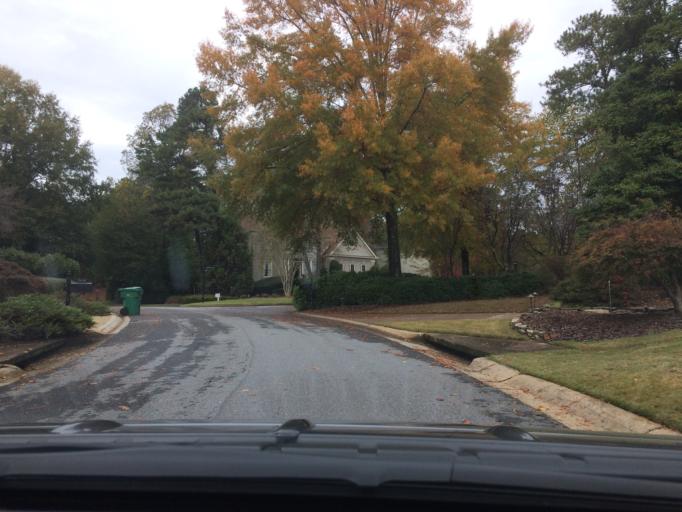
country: US
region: Georgia
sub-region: Fulton County
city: Johns Creek
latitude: 34.0092
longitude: -84.2472
